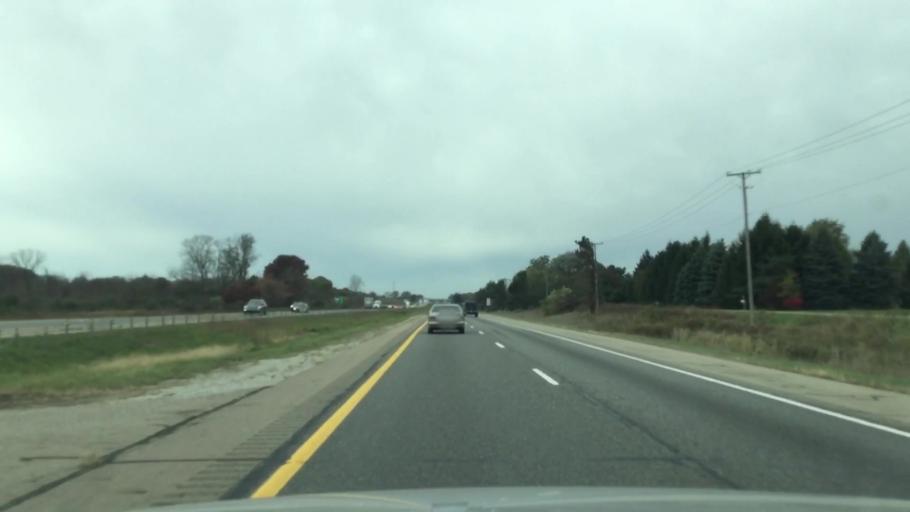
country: US
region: Michigan
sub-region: Washtenaw County
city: Chelsea
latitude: 42.2972
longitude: -83.9861
